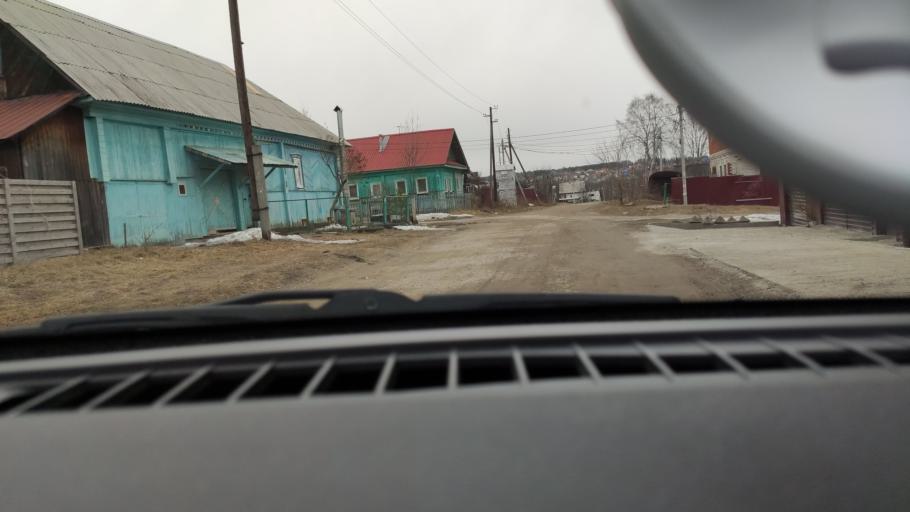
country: RU
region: Perm
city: Kondratovo
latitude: 58.0499
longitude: 56.0418
